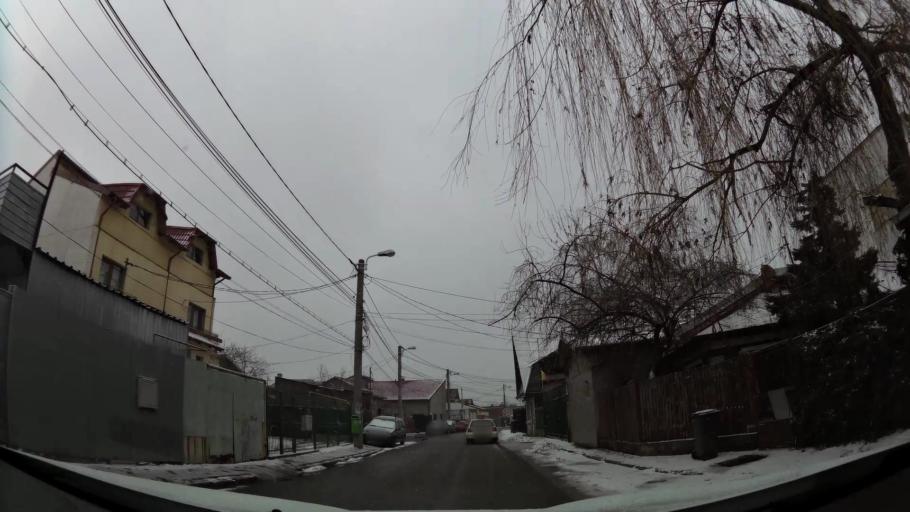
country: RO
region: Prahova
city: Ploiesti
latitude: 44.9445
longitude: 26.0023
